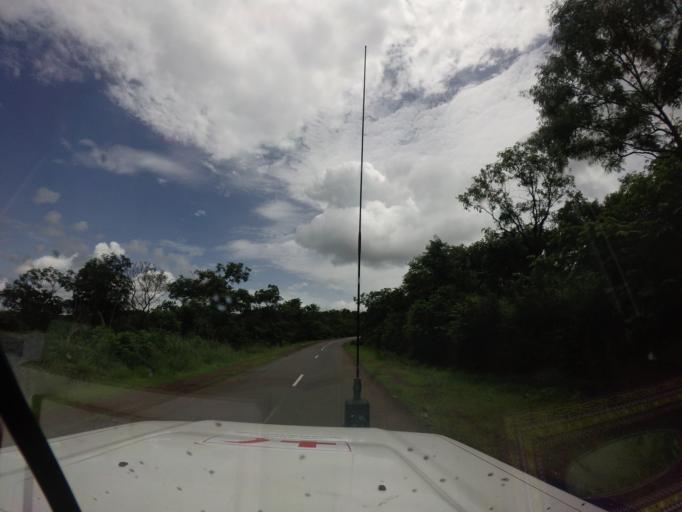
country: GN
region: Faranah
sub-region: Faranah Prefecture
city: Faranah
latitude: 10.0251
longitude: -10.9766
